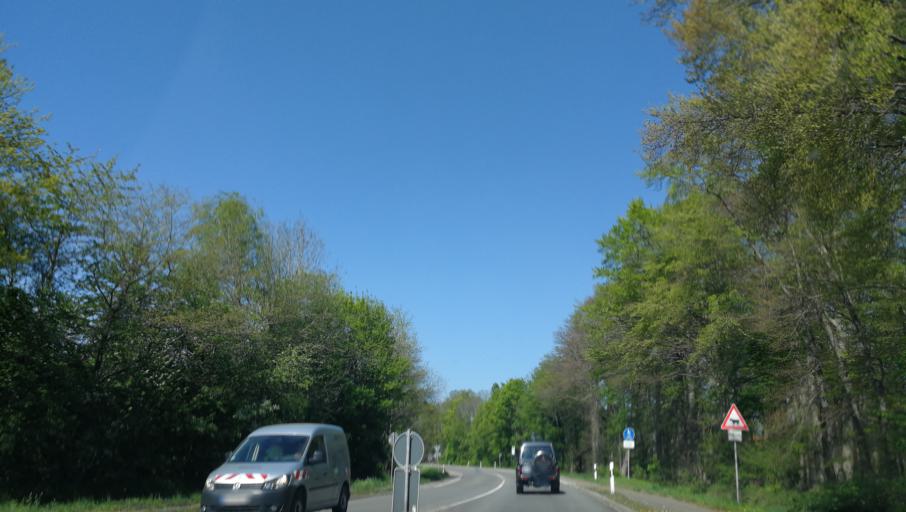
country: DE
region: North Rhine-Westphalia
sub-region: Regierungsbezirk Munster
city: Steinfurt
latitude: 52.1696
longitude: 7.3455
